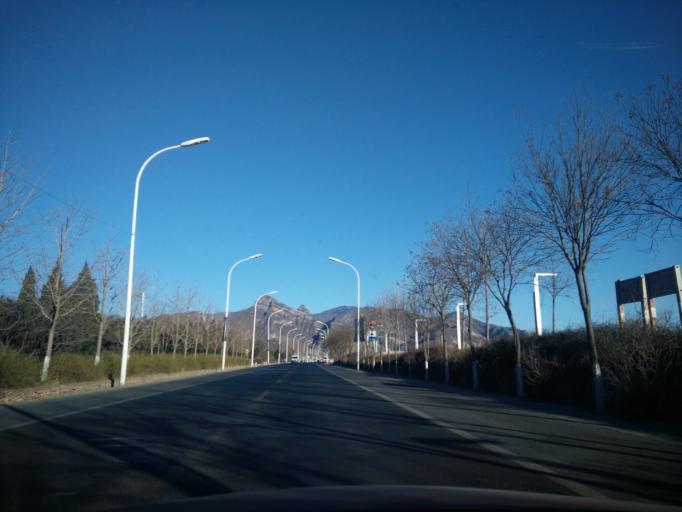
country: CN
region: Beijing
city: Junzhuang
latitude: 39.9774
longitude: 116.0841
